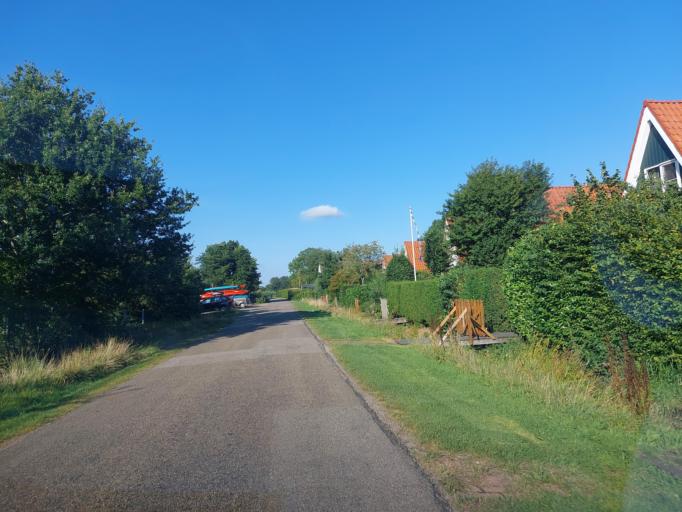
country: NL
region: Friesland
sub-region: Gemeente Skarsterlan
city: Joure
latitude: 53.0136
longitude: 5.7720
